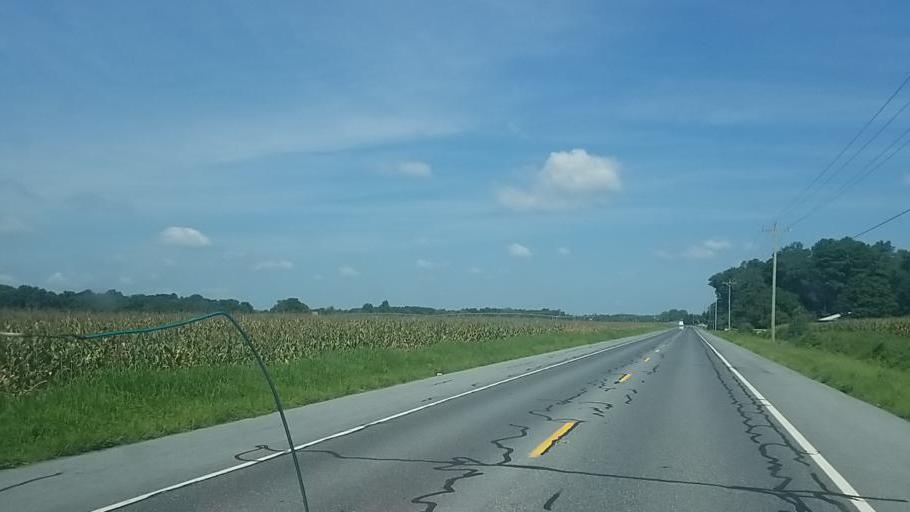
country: US
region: Delaware
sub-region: Sussex County
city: Seaford
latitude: 38.6796
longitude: -75.5825
